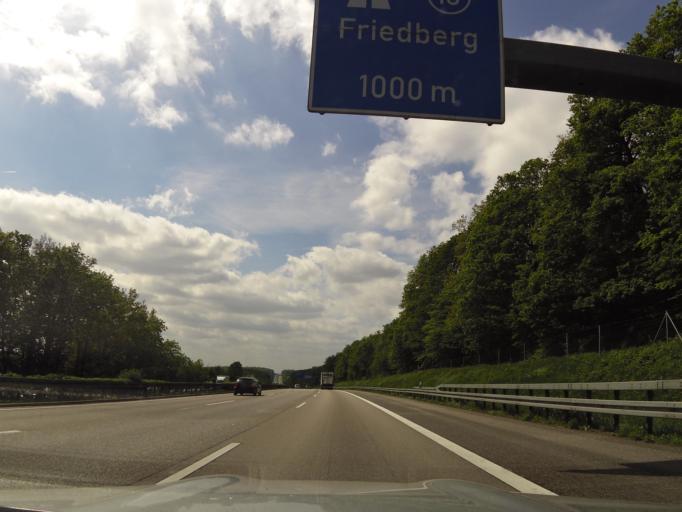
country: DE
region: Hesse
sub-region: Regierungsbezirk Darmstadt
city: Rosbach vor der Hohe
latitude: 50.3002
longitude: 8.6748
